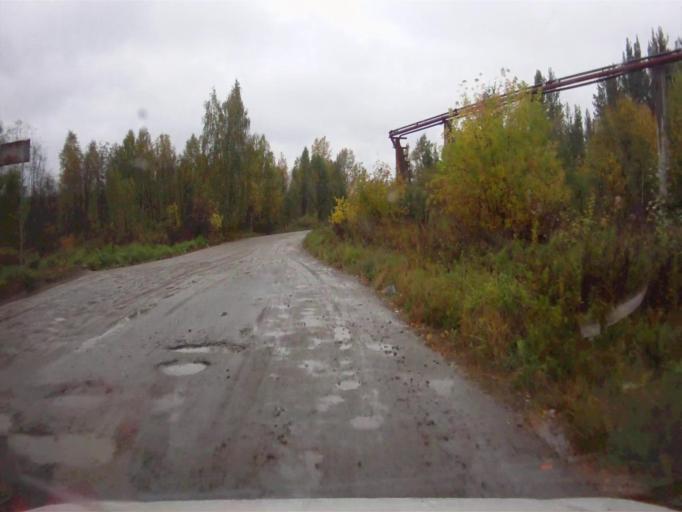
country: RU
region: Chelyabinsk
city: Kyshtym
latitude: 55.7296
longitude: 60.5201
